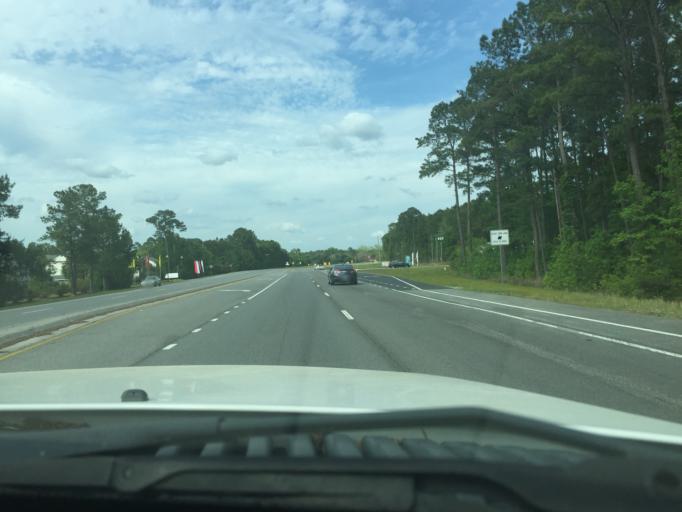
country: US
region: Georgia
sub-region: Chatham County
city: Georgetown
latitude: 31.9917
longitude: -81.2756
